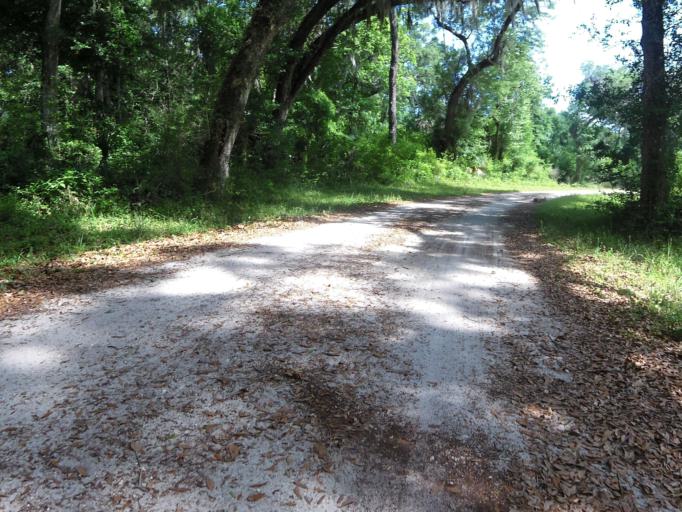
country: US
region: Florida
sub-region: Saint Johns County
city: Palm Valley
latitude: 30.1339
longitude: -81.3676
